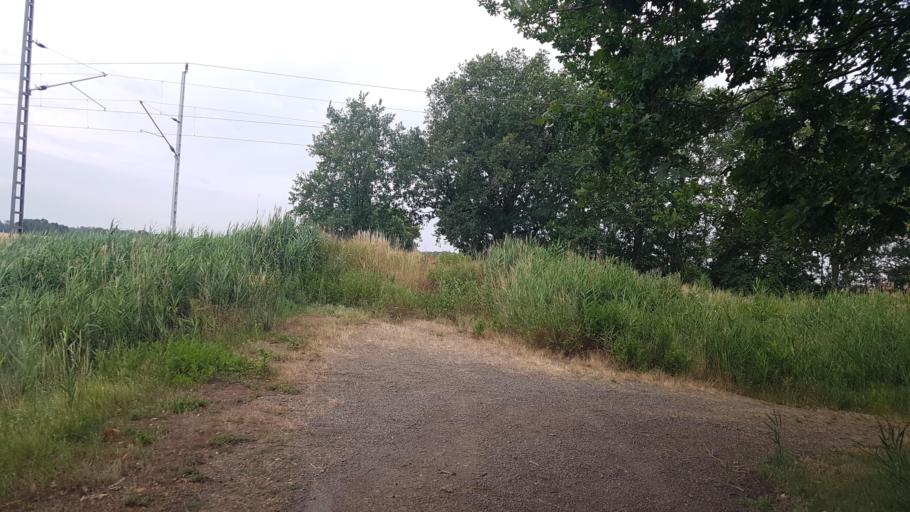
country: DE
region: Saxony-Anhalt
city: Annaburg
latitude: 51.7568
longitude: 13.0008
